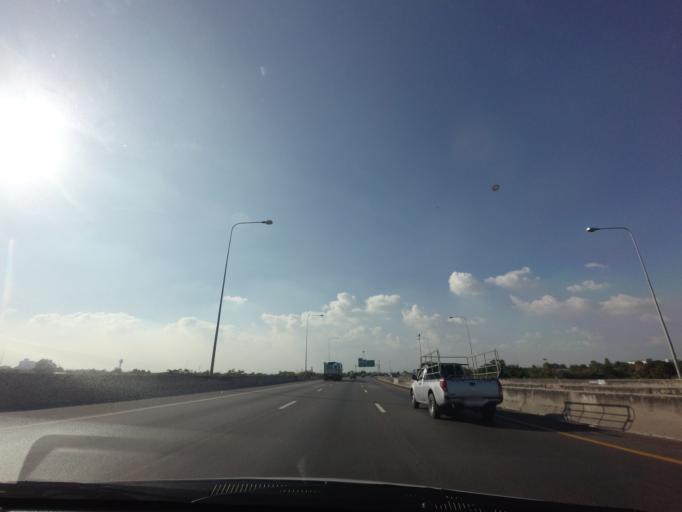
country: TH
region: Samut Prakan
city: Samut Prakan
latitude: 13.6043
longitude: 100.6295
